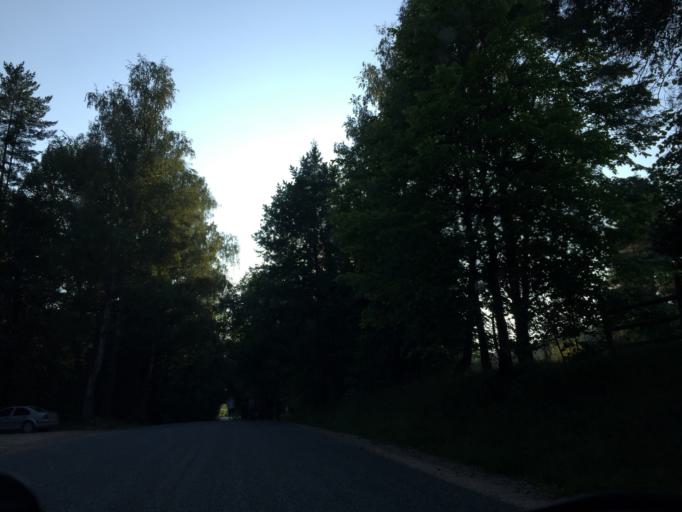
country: LV
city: Tervete
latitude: 56.4797
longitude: 23.3773
